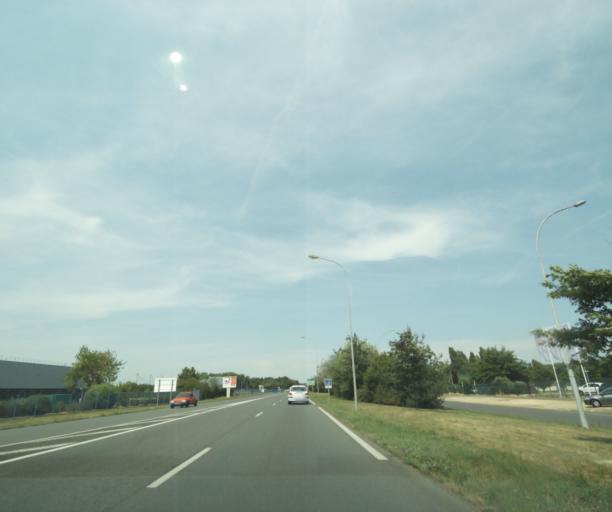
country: FR
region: Poitou-Charentes
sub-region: Departement de la Vienne
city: Antran
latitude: 46.8470
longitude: 0.5502
